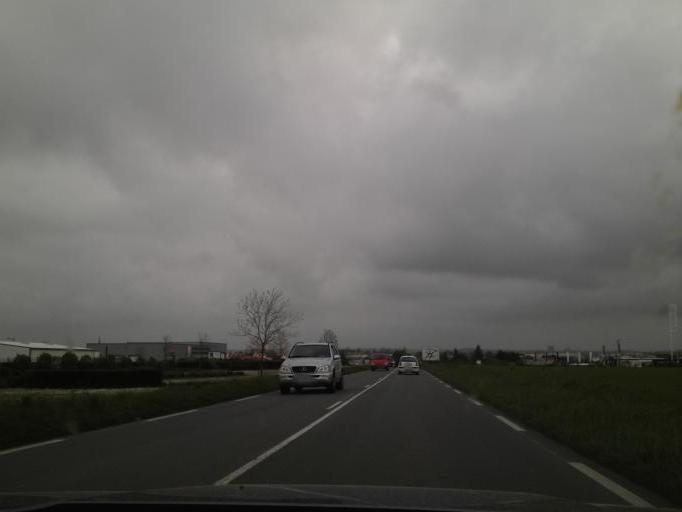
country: FR
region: Pays de la Loire
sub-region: Departement de la Vendee
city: Fontenay-le-Comte
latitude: 46.4448
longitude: -0.8158
